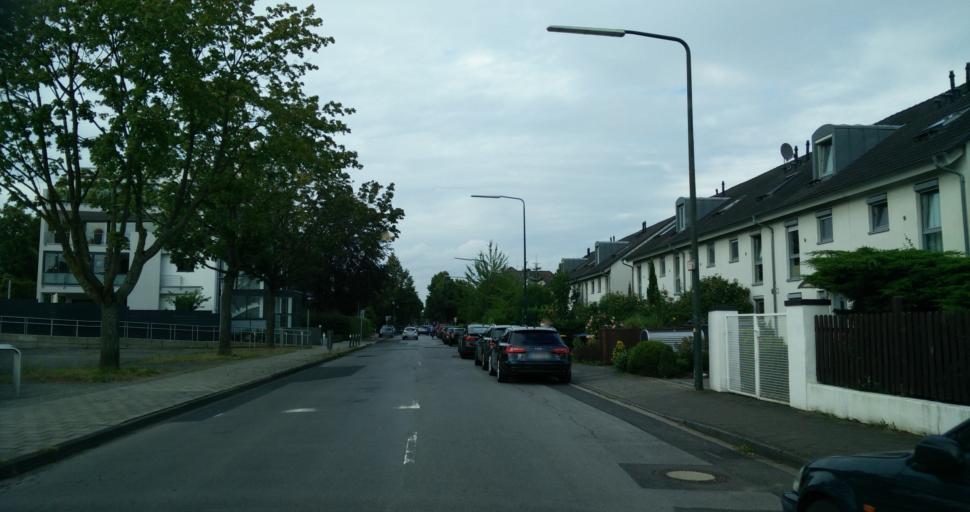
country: DE
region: North Rhine-Westphalia
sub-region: Regierungsbezirk Dusseldorf
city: Meerbusch
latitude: 51.2892
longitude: 6.7392
